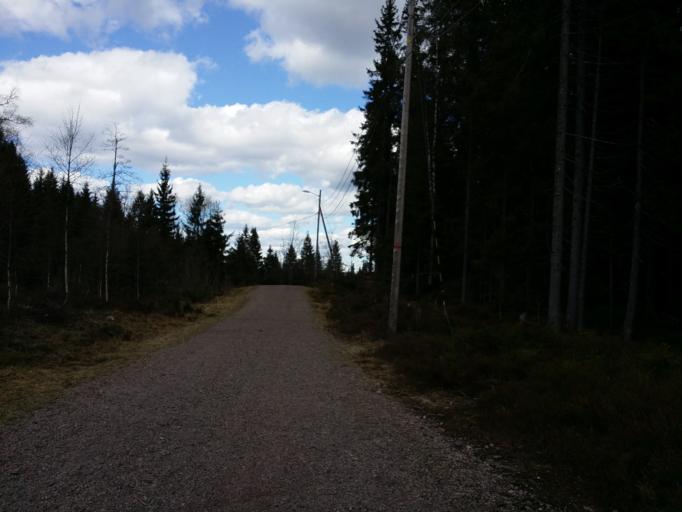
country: NO
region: Oslo
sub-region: Oslo
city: Sjolyststranda
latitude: 59.9869
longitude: 10.6977
